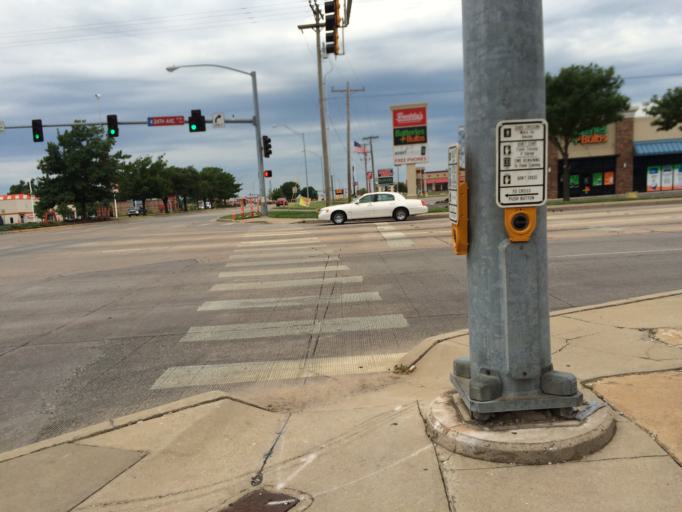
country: US
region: Oklahoma
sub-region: Cleveland County
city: Norman
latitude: 35.2187
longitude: -97.4764
